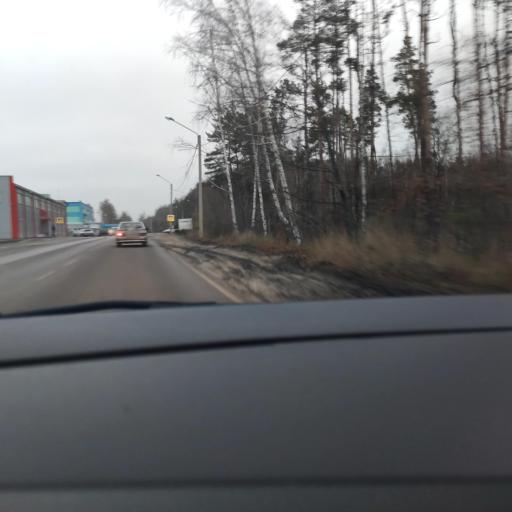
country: RU
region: Voronezj
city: Somovo
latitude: 51.7185
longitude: 39.2944
